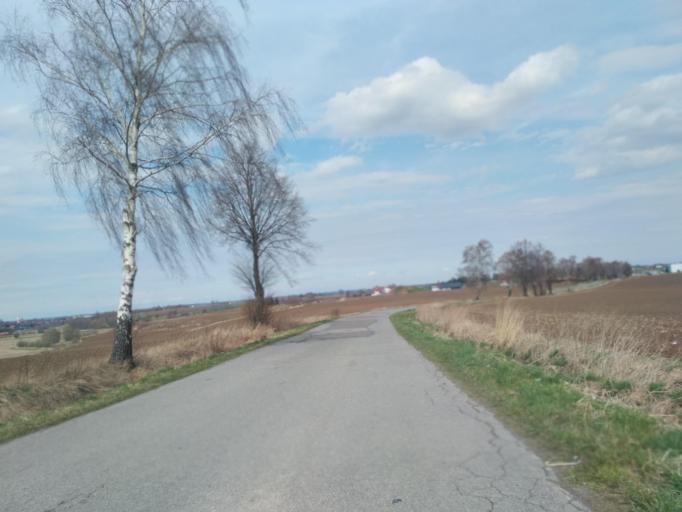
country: PL
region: Subcarpathian Voivodeship
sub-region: Powiat ropczycko-sedziszowski
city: Sedziszow Malopolski
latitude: 50.0531
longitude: 21.7148
